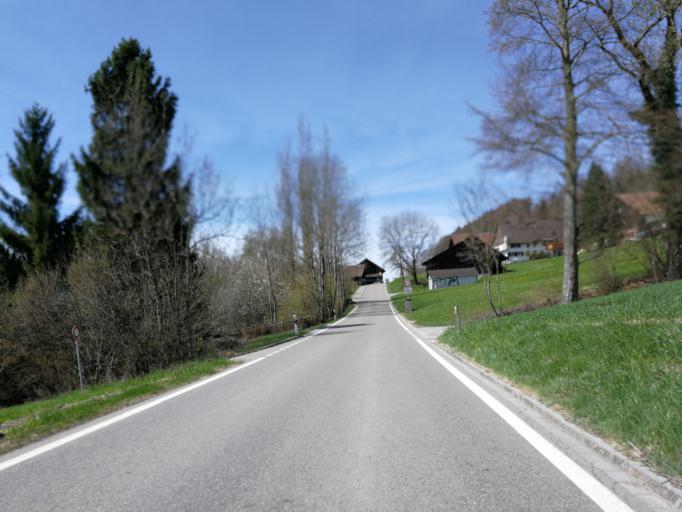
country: CH
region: Zurich
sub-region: Bezirk Meilen
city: Obermeilen
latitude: 47.2848
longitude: 8.6714
